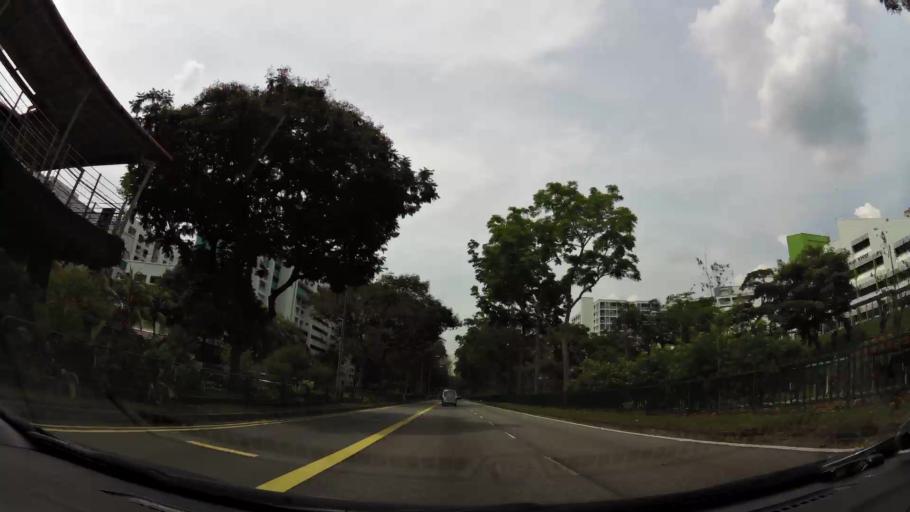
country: MY
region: Johor
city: Johor Bahru
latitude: 1.3789
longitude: 103.7693
